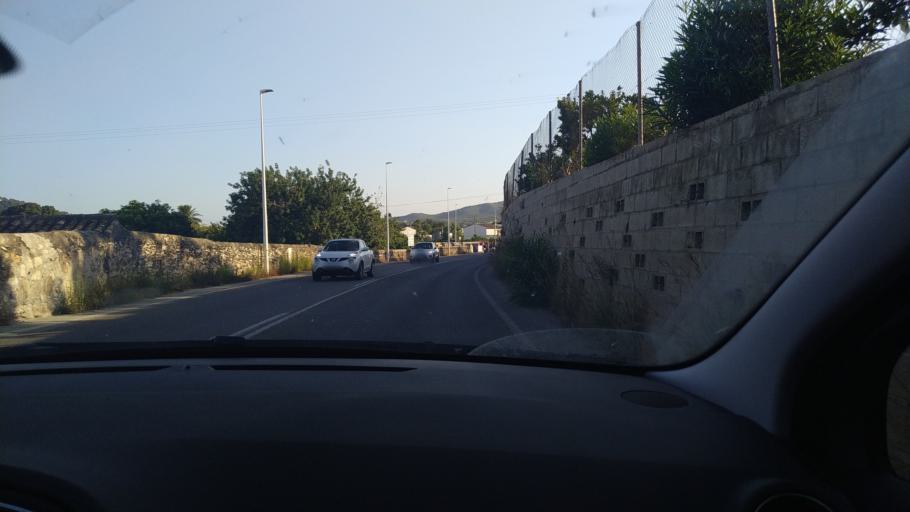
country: ES
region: Valencia
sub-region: Provincia de Alicante
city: Javea
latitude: 38.7824
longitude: 0.1561
